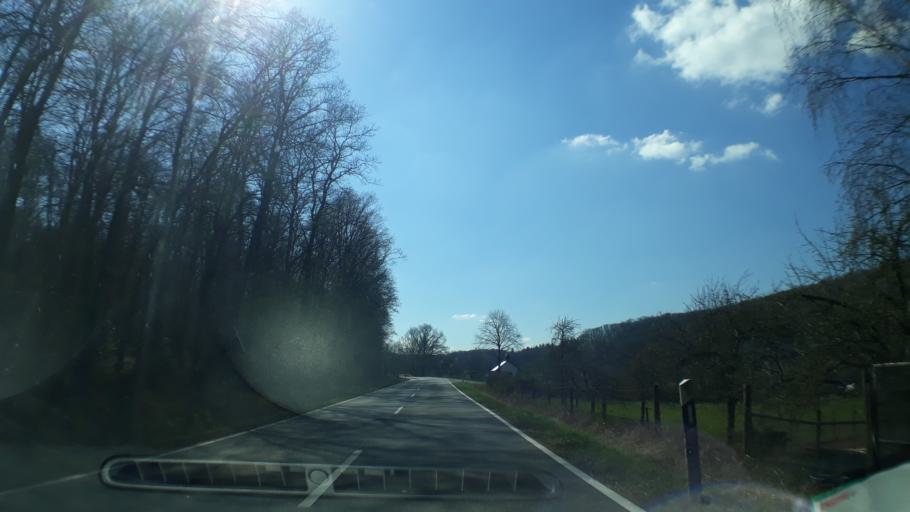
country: DE
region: North Rhine-Westphalia
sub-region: Regierungsbezirk Koln
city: Mechernich
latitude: 50.6007
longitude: 6.6832
